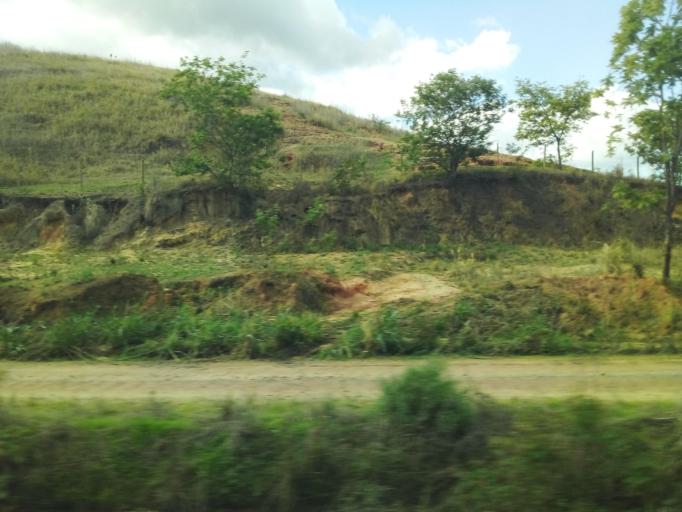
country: BR
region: Minas Gerais
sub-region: Conselheiro Pena
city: Conselheiro Pena
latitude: -18.9832
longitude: -41.6123
